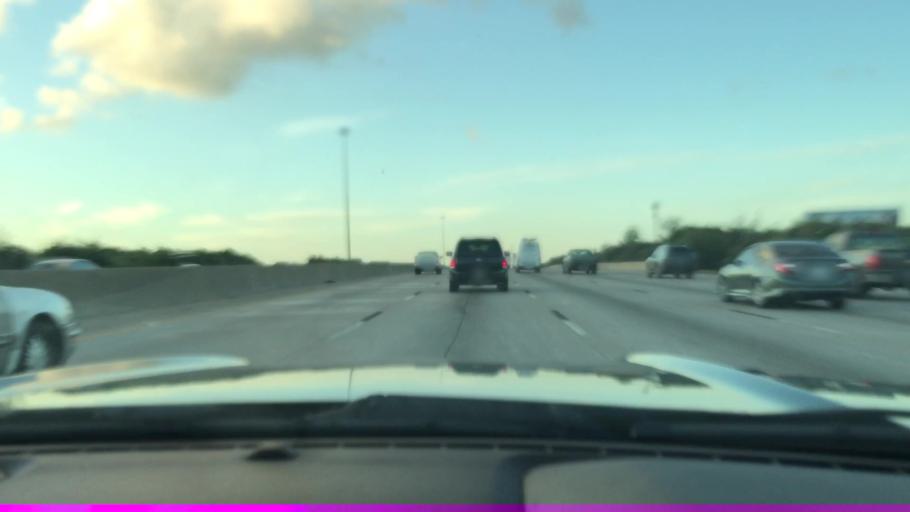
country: US
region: Texas
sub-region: Harris County
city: Jacinto City
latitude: 29.7477
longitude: -95.2650
